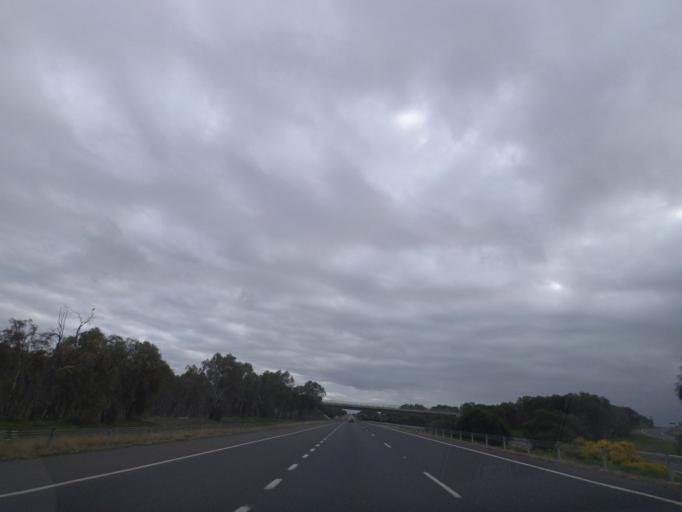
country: AU
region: New South Wales
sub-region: Corowa Shire
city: Howlong
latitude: -36.0825
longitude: 146.7305
